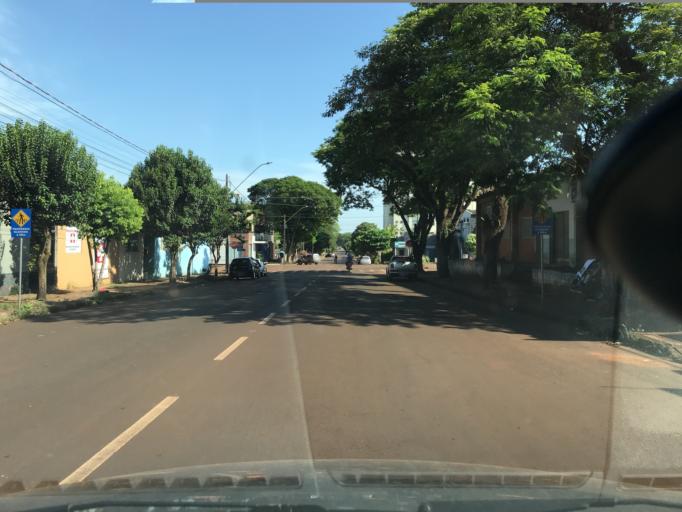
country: BR
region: Parana
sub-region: Palotina
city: Palotina
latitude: -24.2845
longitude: -53.8421
